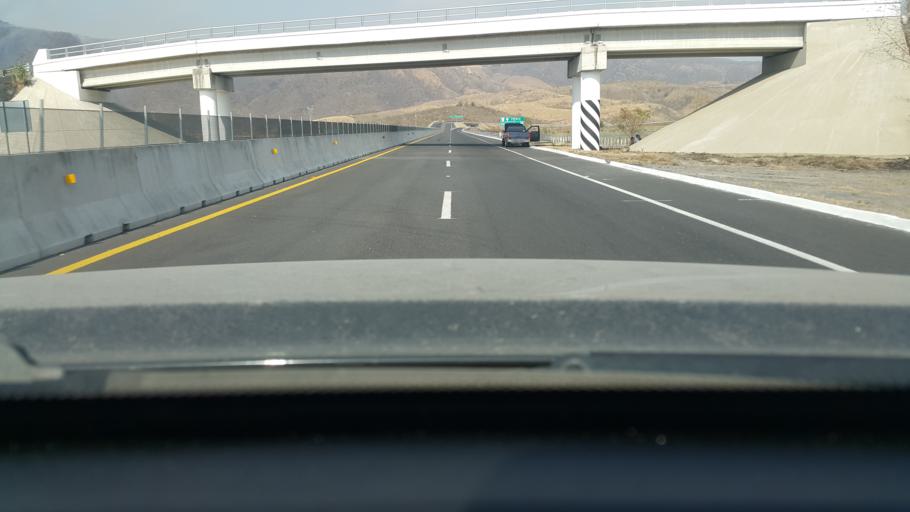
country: MX
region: Nayarit
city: Jala
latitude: 21.0787
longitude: -104.4331
